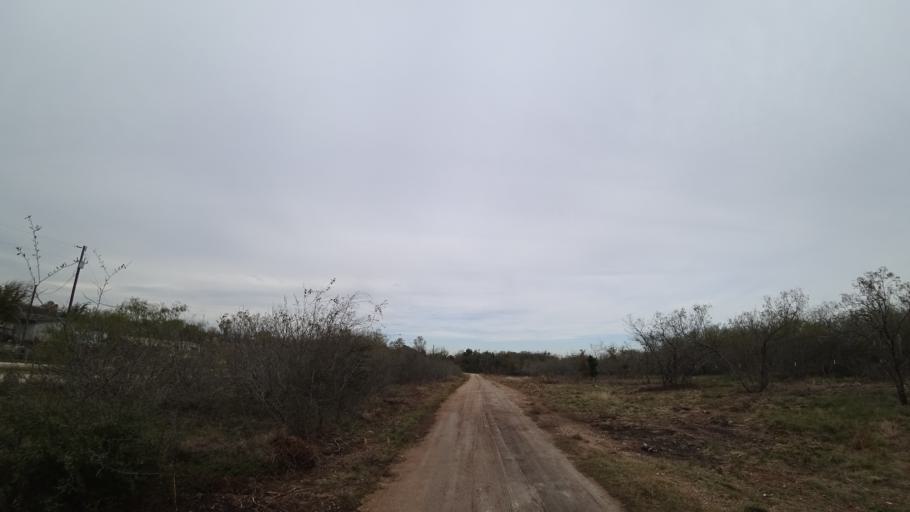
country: US
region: Texas
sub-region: Travis County
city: Garfield
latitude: 30.1073
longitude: -97.5861
